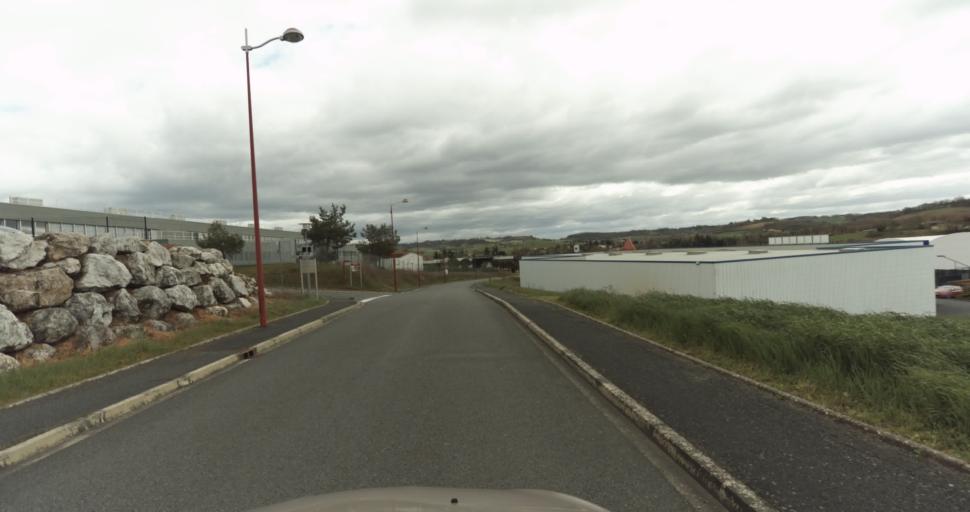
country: FR
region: Midi-Pyrenees
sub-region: Departement du Tarn
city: Puygouzon
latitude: 43.8938
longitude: 2.1643
